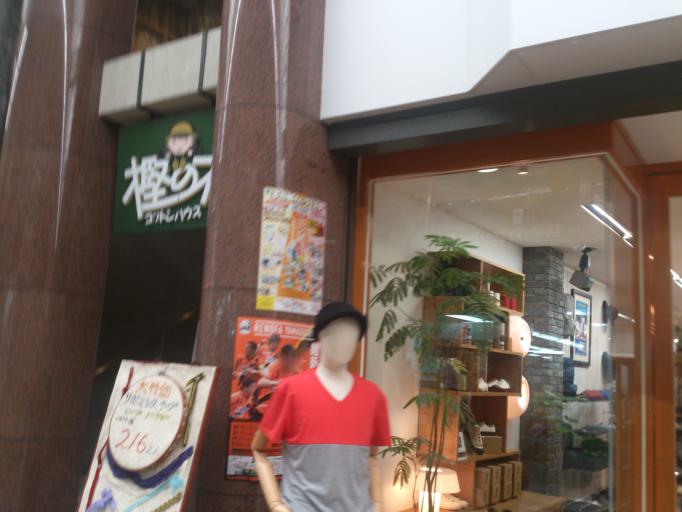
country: JP
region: Yamaguchi
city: Yamaguchi-shi
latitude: 34.1760
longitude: 131.4765
